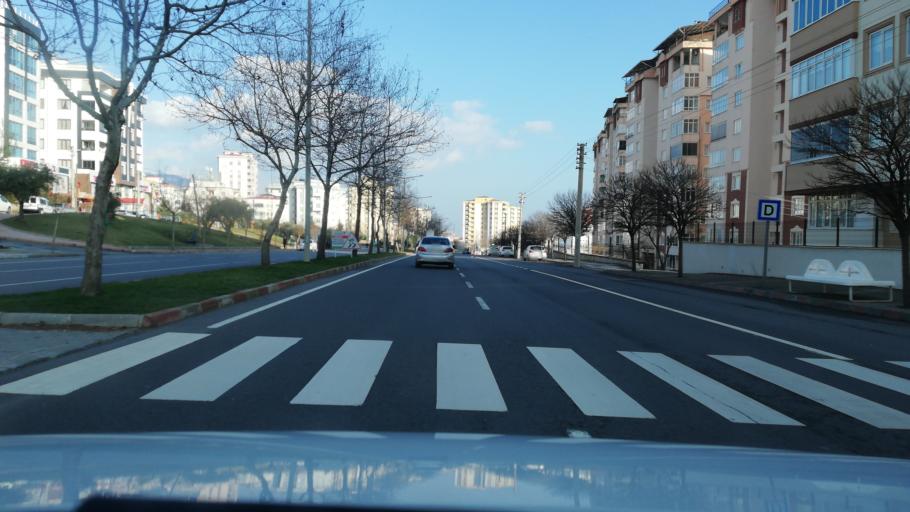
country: TR
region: Kahramanmaras
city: Kahramanmaras
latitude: 37.5956
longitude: 36.8888
